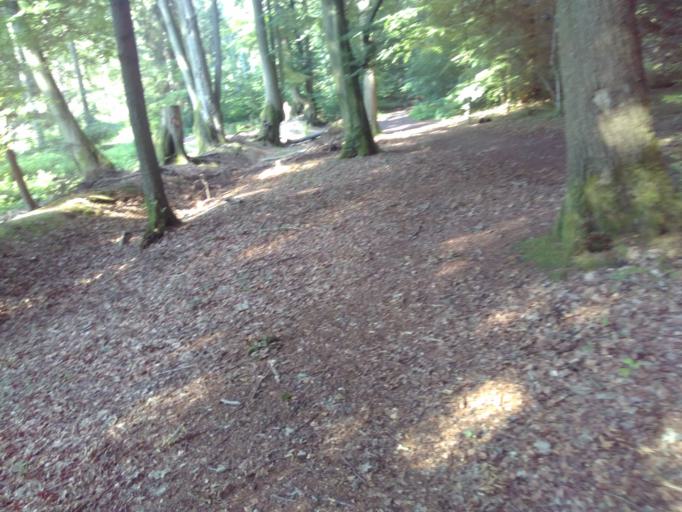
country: DE
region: North Rhine-Westphalia
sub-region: Regierungsbezirk Koln
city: Aachen
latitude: 50.7224
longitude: 6.0970
